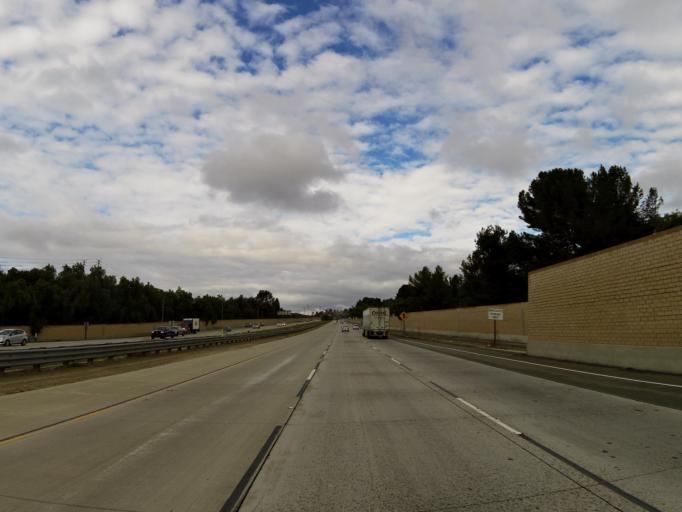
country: US
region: California
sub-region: Ventura County
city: Thousand Oaks
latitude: 34.2131
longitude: -118.8492
